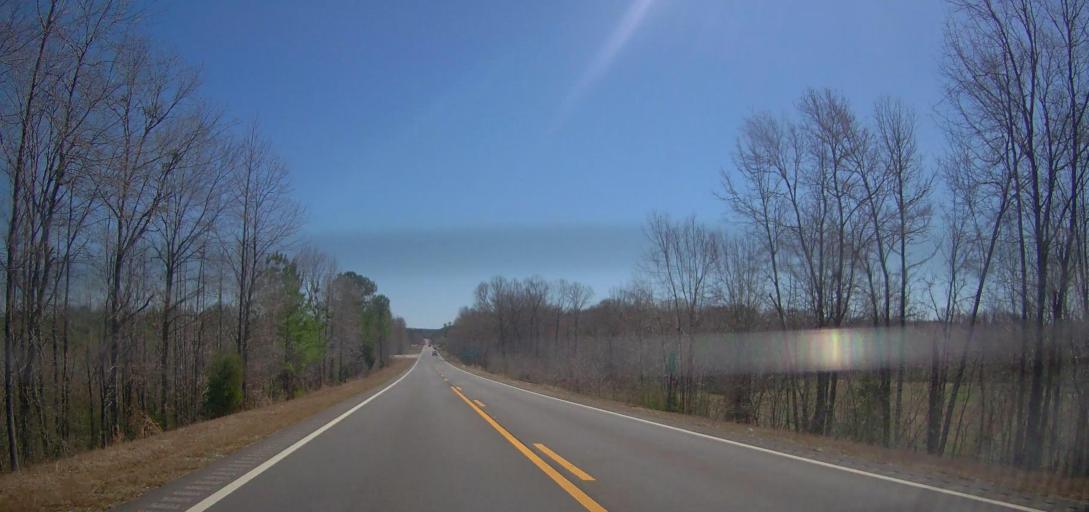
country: US
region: Alabama
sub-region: Calhoun County
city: Ohatchee
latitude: 33.7809
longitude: -86.0054
